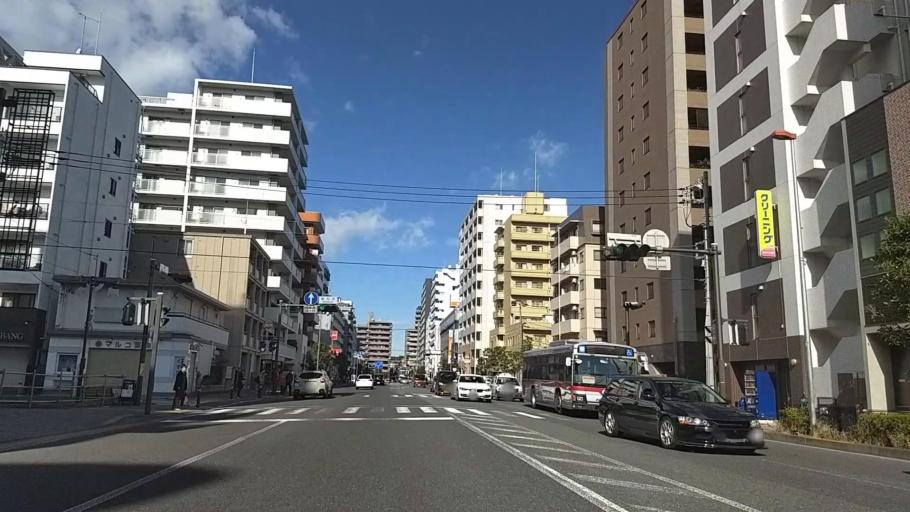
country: JP
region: Kanagawa
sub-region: Kawasaki-shi
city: Kawasaki
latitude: 35.5800
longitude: 139.6639
